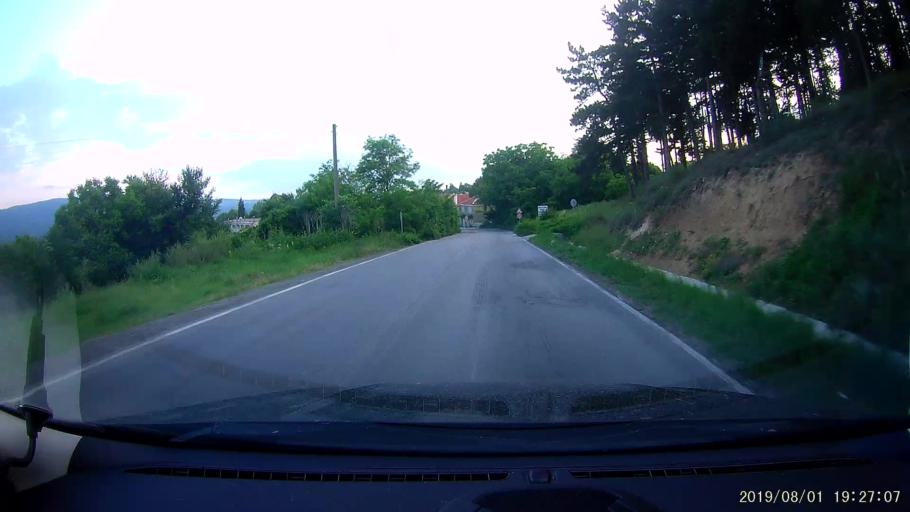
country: BG
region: Burgas
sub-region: Obshtina Sungurlare
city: Sungurlare
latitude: 42.8519
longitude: 26.9321
